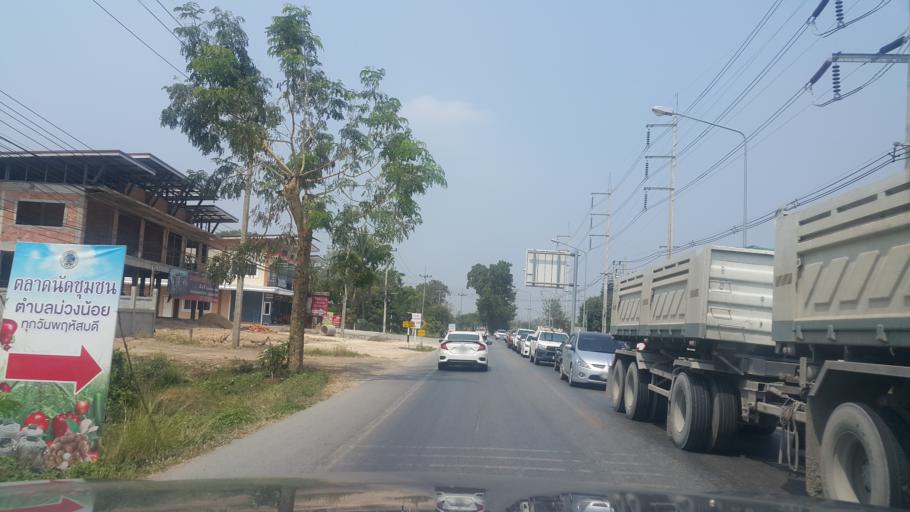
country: TH
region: Lamphun
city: Pa Sang
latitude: 18.4730
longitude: 98.9523
